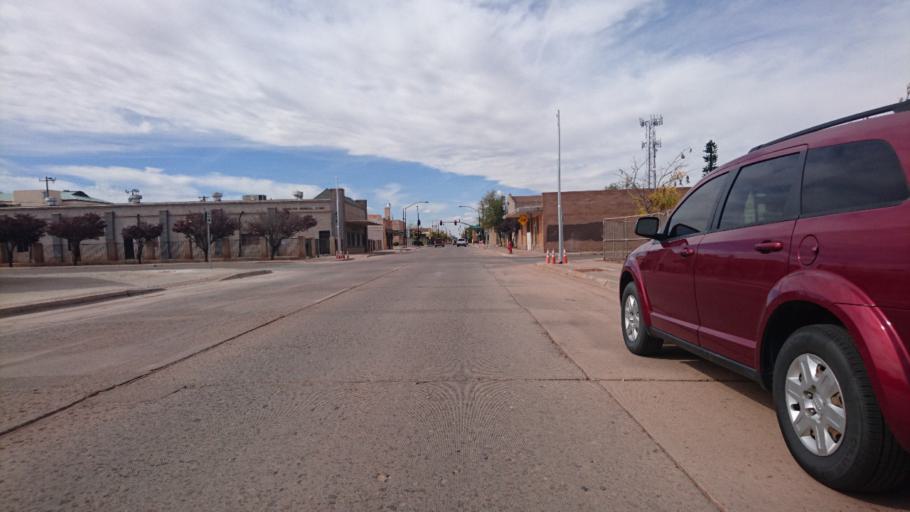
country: US
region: Arizona
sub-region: Navajo County
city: Winslow
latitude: 35.0233
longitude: -110.6951
